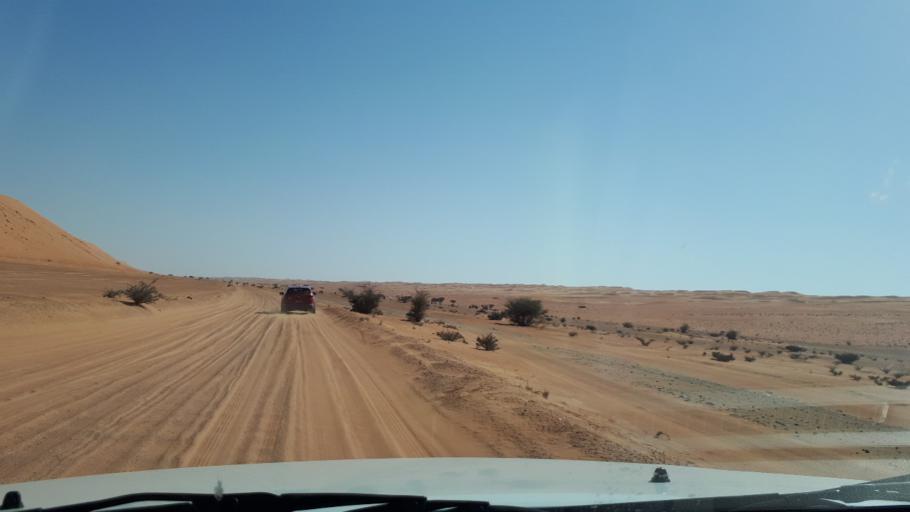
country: OM
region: Ash Sharqiyah
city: Badiyah
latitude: 22.4553
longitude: 58.7392
